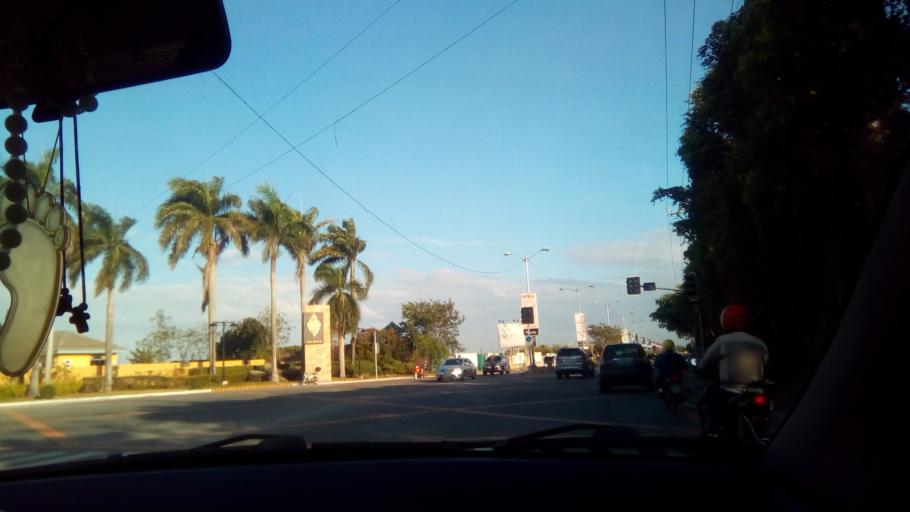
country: PH
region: Calabarzon
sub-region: Province of Laguna
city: San Pedro
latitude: 14.3845
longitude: 121.0107
